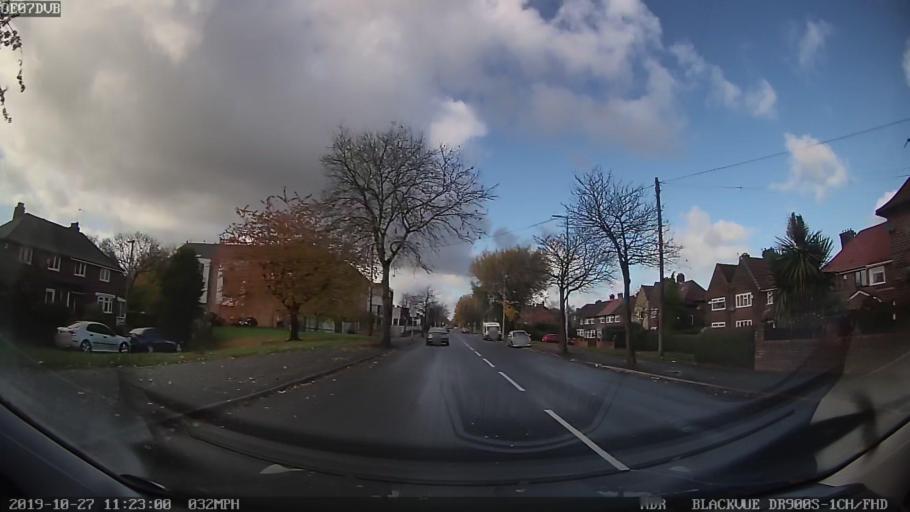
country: GB
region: England
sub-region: Manchester
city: Blackley
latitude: 53.5230
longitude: -2.1889
